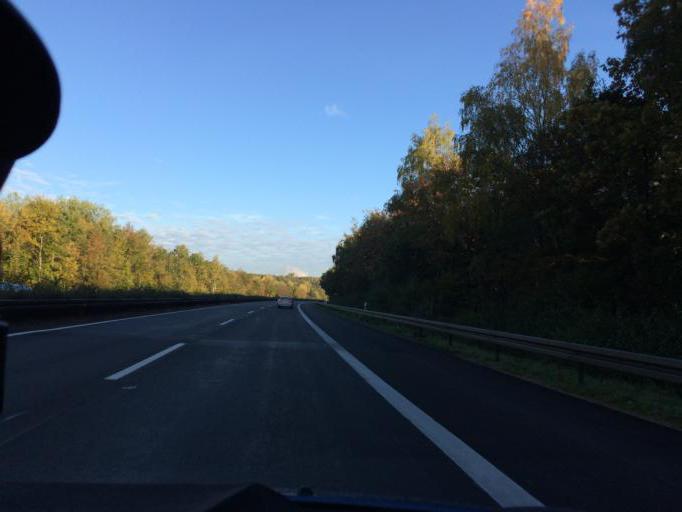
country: DE
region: North Rhine-Westphalia
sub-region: Regierungsbezirk Koln
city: Frechen
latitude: 50.8729
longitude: 6.8023
